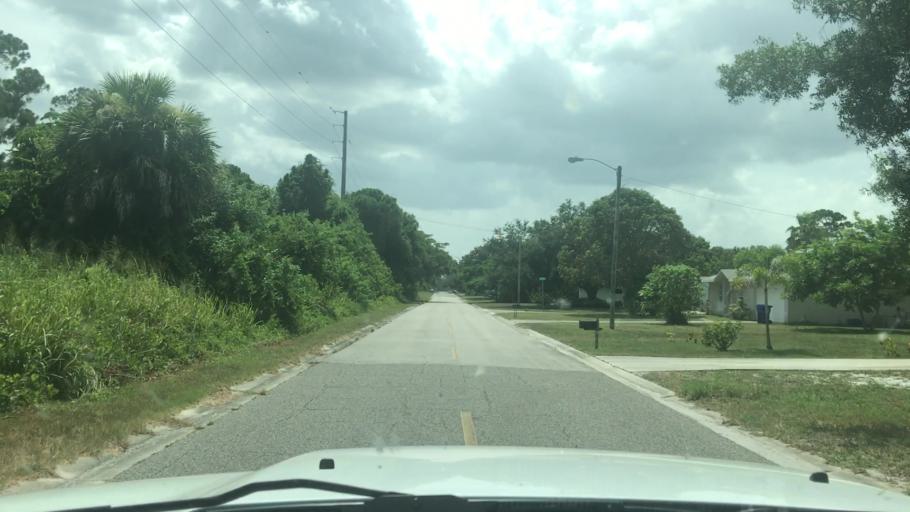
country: US
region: Florida
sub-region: Saint Lucie County
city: Lakewood Park
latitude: 27.5580
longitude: -80.3881
